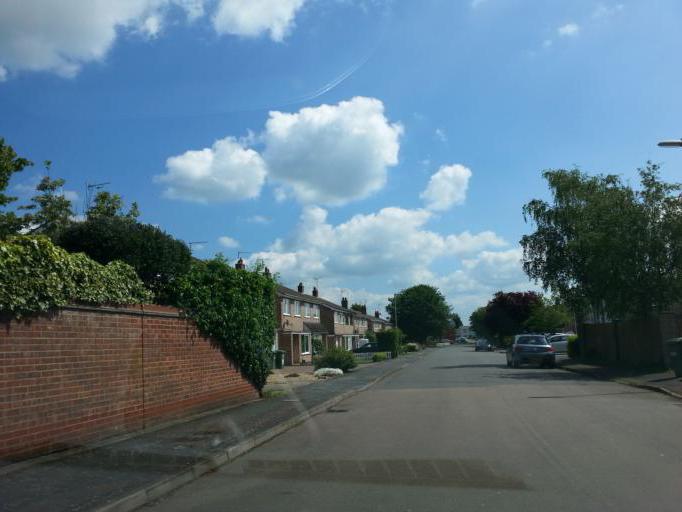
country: GB
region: England
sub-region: Cambridgeshire
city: Stilton
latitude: 52.4924
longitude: -0.2938
